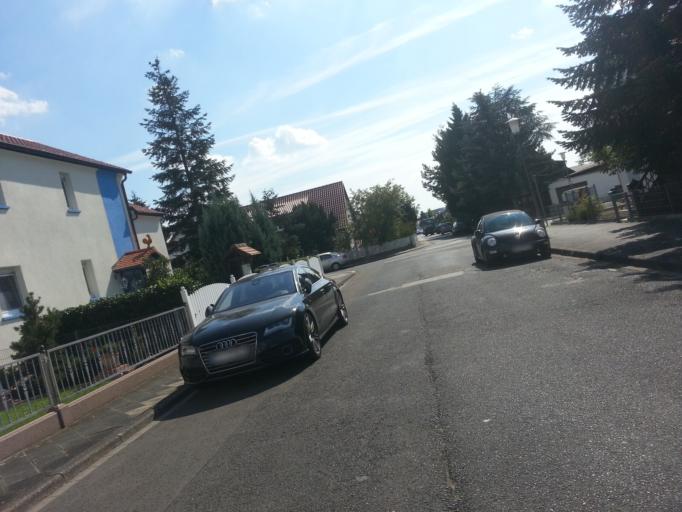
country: DE
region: Baden-Wuerttemberg
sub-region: Karlsruhe Region
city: Mannheim
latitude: 49.5425
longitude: 8.4799
